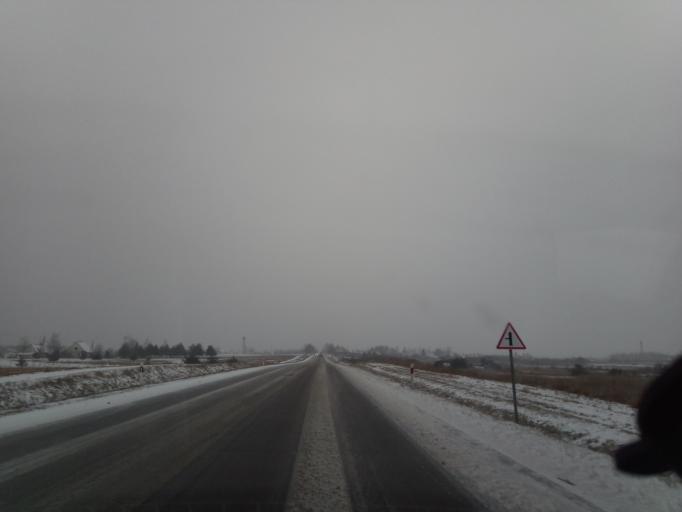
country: LT
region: Vilnius County
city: Ukmerge
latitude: 55.3175
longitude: 24.8735
